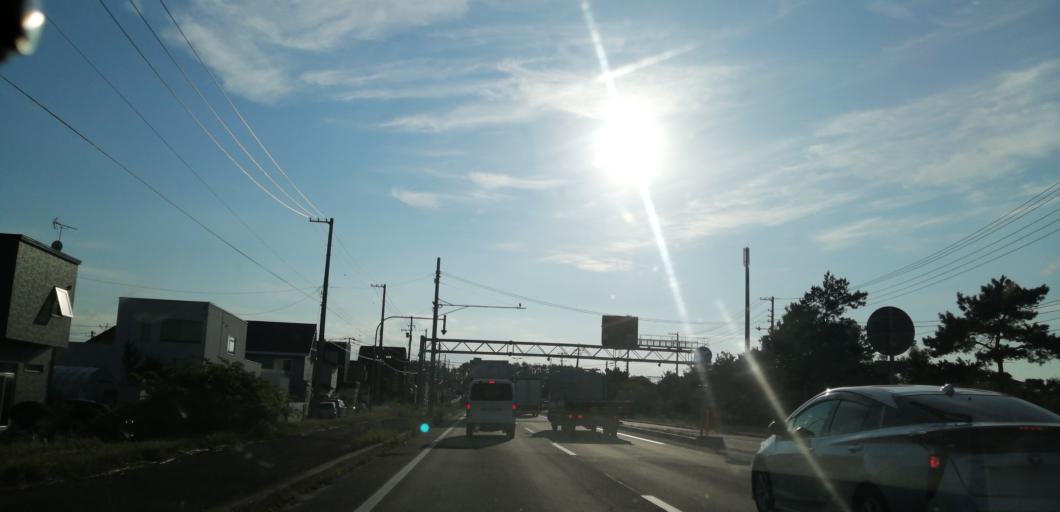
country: JP
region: Hokkaido
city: Kitahiroshima
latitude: 42.9971
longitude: 141.5689
